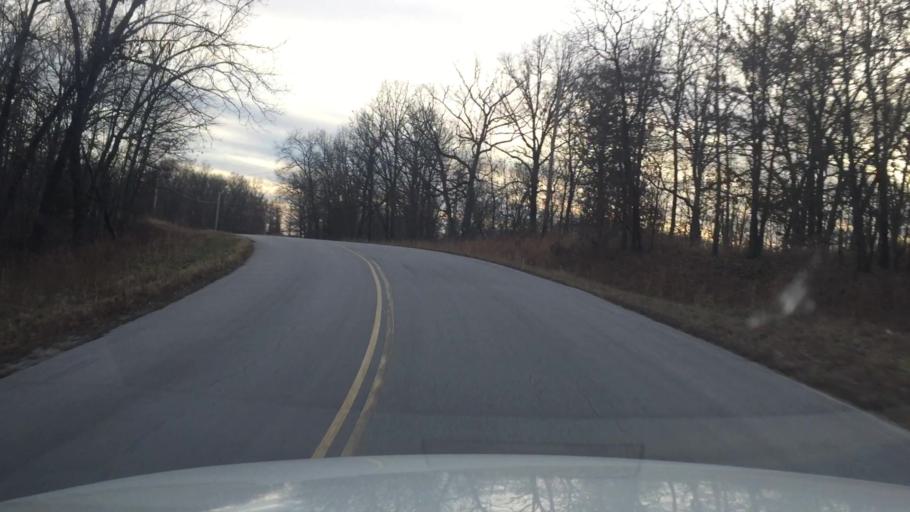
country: US
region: Missouri
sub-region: Morgan County
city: Versailles
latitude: 38.3300
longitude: -92.7754
